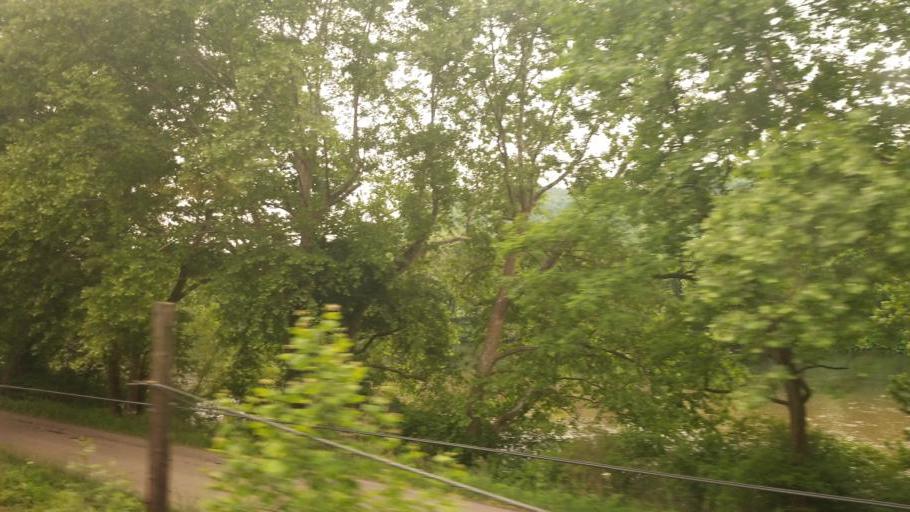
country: US
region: Pennsylvania
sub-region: Fayette County
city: South Connellsville
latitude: 39.8263
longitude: -79.3695
